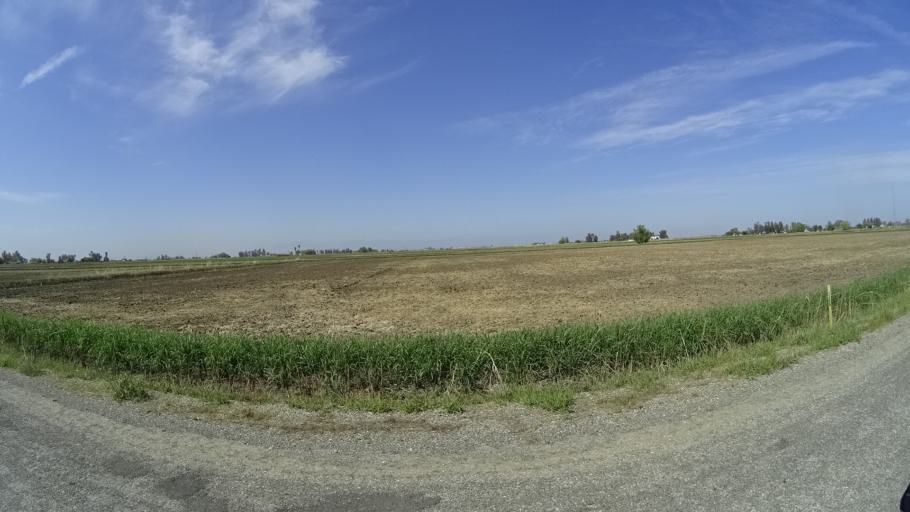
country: US
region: California
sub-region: Glenn County
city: Hamilton City
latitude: 39.5897
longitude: -122.0461
